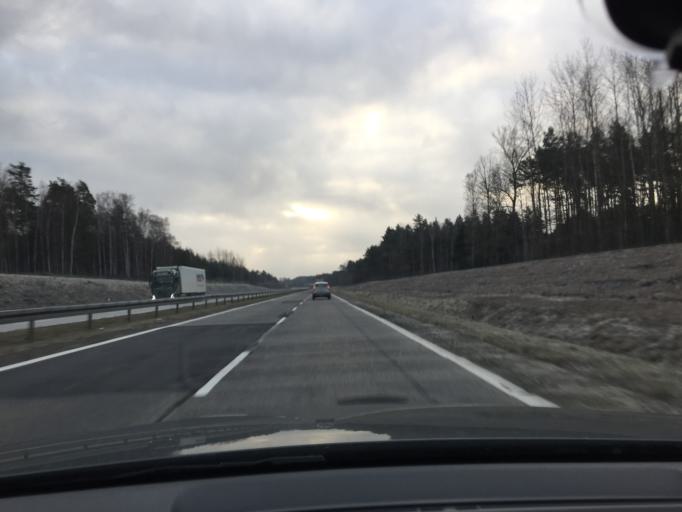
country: PL
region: Lubusz
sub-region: Powiat zarski
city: Sieniawa Zarska
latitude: 51.5751
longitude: 15.0315
